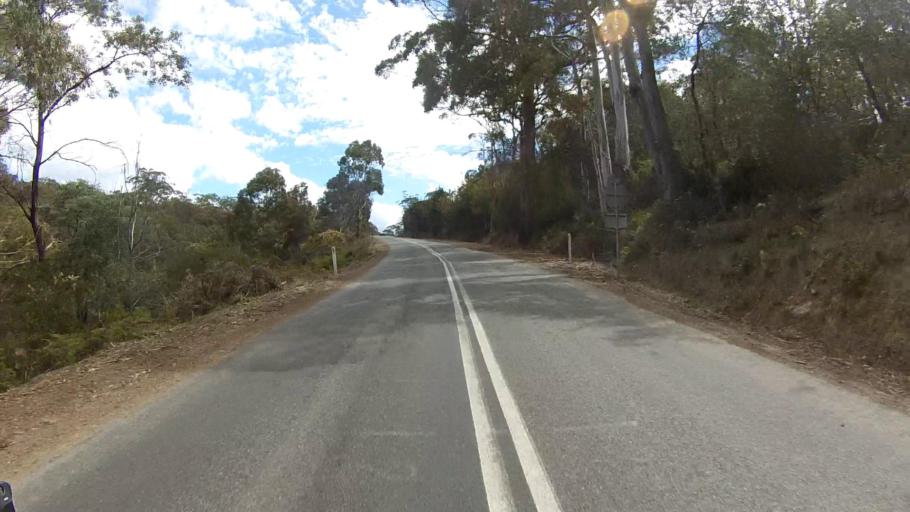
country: AU
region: Tasmania
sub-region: Break O'Day
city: St Helens
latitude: -41.9761
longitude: 148.1471
